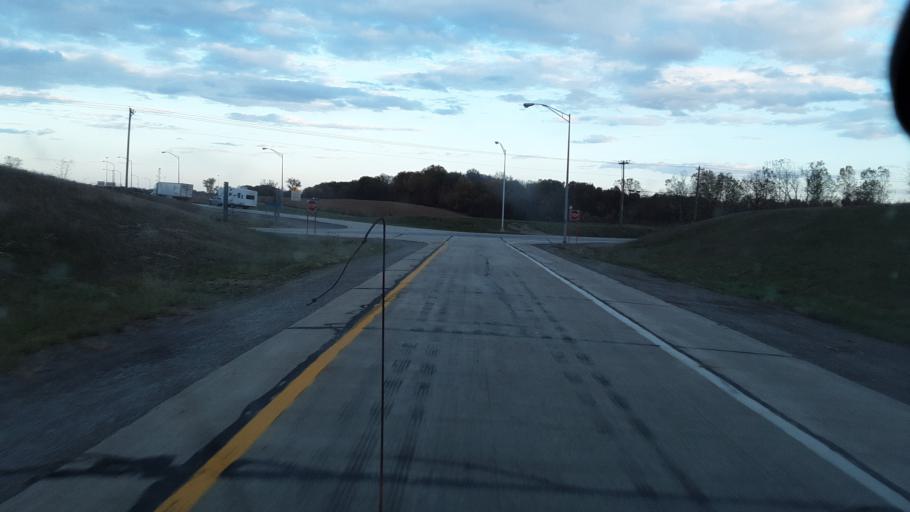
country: US
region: Ohio
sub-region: Williams County
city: Montpelier
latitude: 41.6289
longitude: -84.7669
